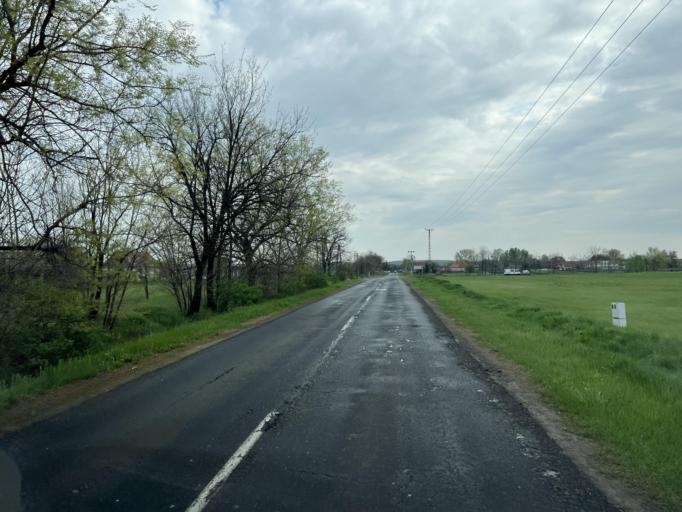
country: HU
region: Pest
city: Albertirsa
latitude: 47.2398
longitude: 19.5940
